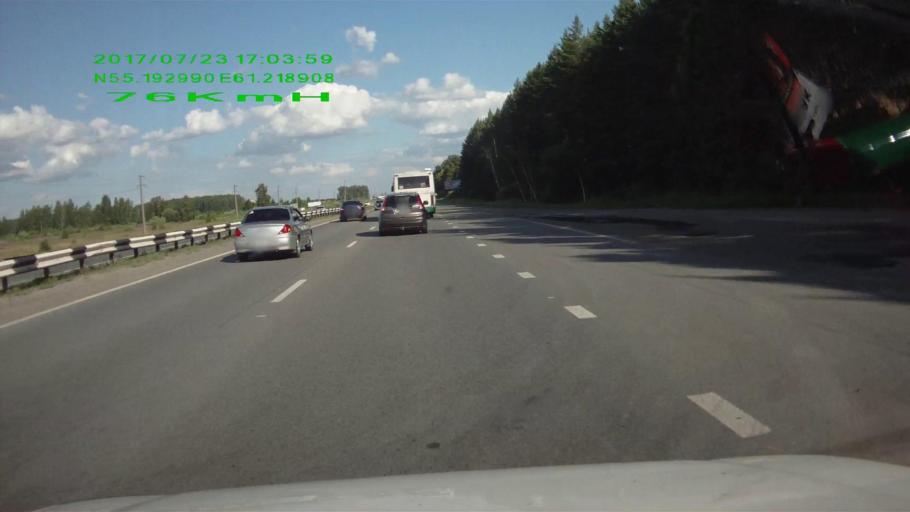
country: RU
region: Chelyabinsk
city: Roshchino
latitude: 55.1927
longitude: 61.2200
